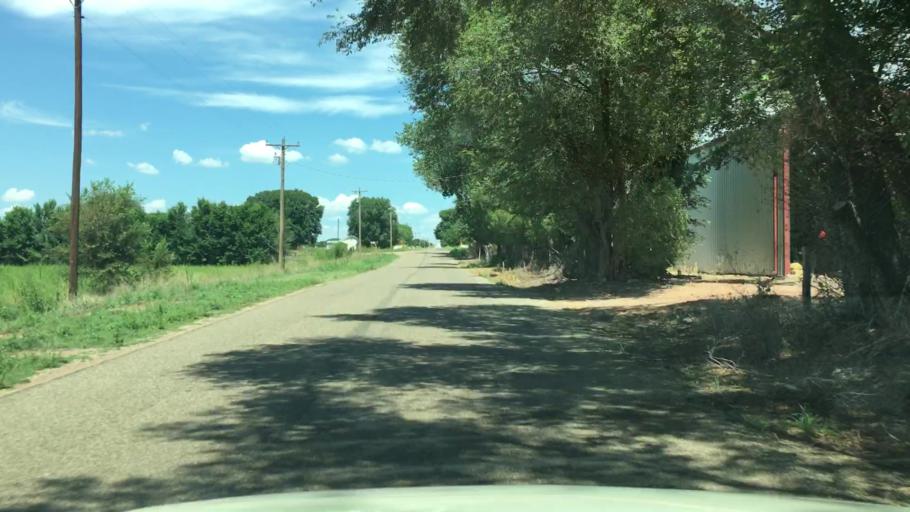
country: US
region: New Mexico
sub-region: De Baca County
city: Fort Sumner
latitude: 34.4385
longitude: -104.1936
